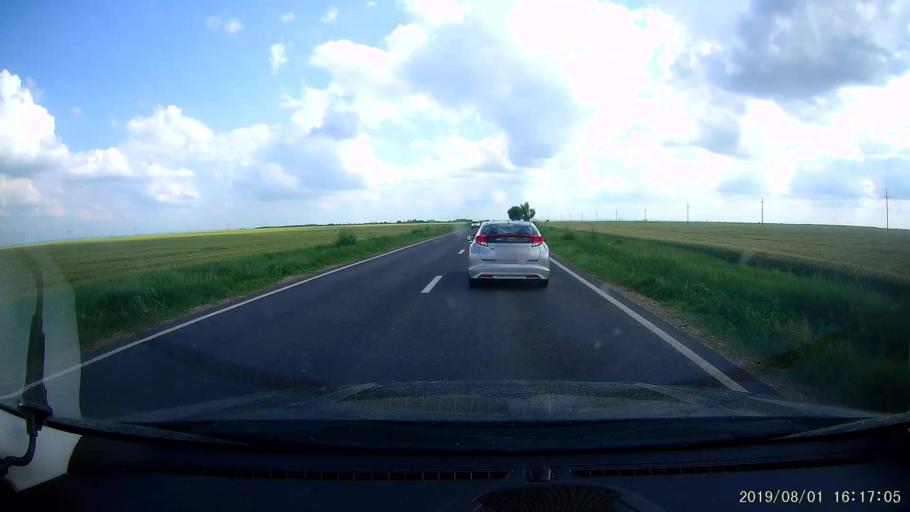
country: RO
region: Calarasi
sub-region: Comuna Stefan Voda
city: Stefan Voda
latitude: 44.3095
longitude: 27.3561
